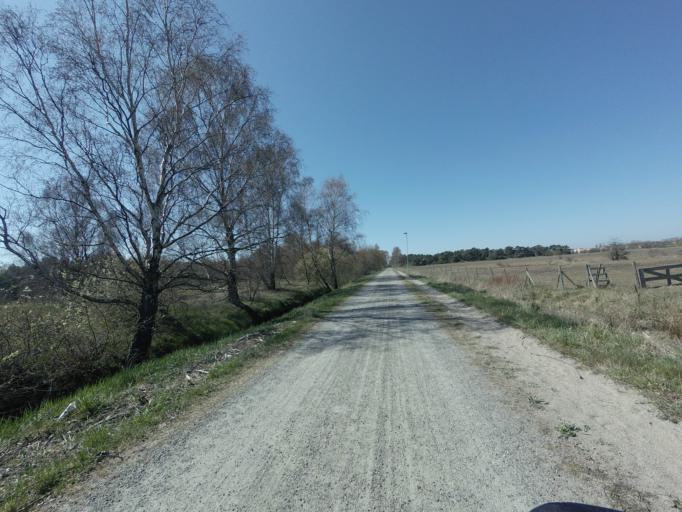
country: SE
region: Skane
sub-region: Vellinge Kommun
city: Skanor med Falsterbo
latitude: 55.4096
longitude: 12.8711
